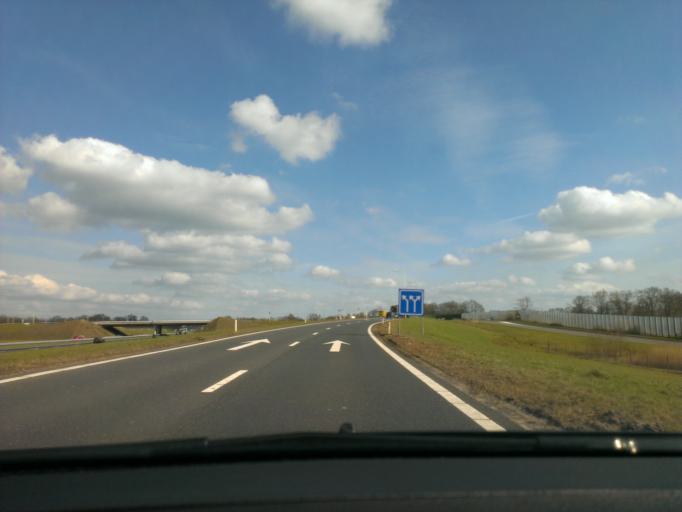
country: NL
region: Overijssel
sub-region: Gemeente Hengelo
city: Hengelo
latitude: 52.2076
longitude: 6.8193
